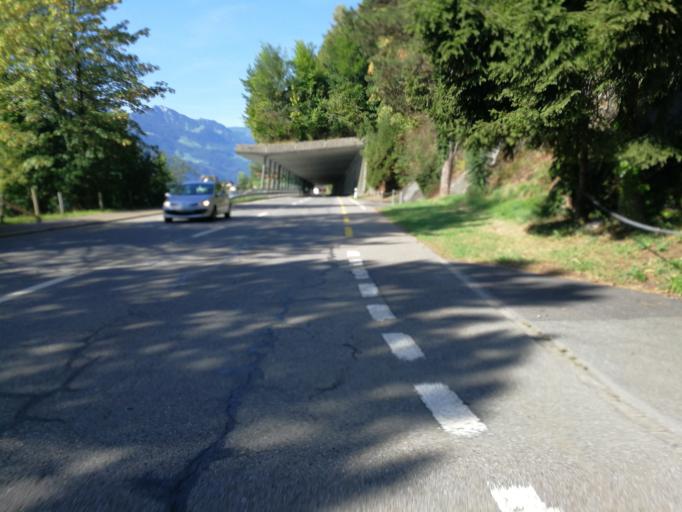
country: CH
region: Schwyz
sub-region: Bezirk Schwyz
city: Ingenbohl
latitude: 46.9996
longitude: 8.5737
